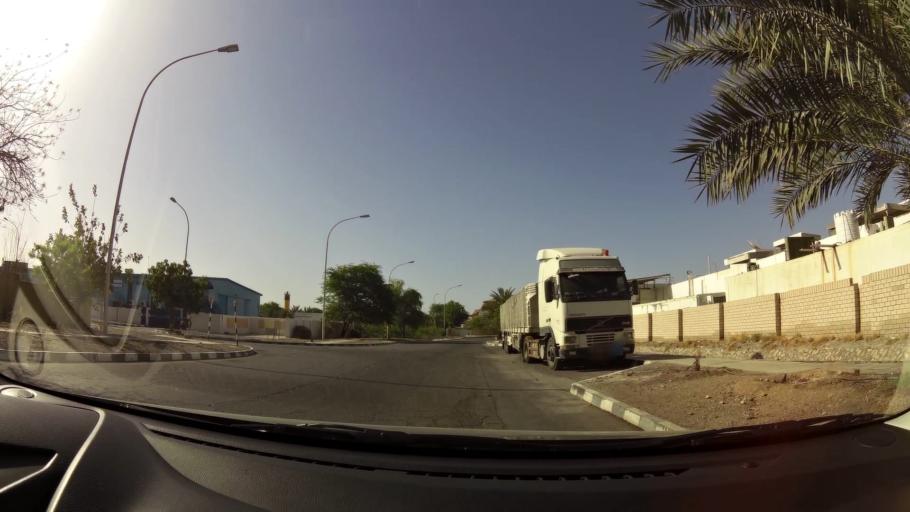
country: OM
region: Muhafazat Masqat
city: As Sib al Jadidah
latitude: 23.5565
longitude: 58.2074
